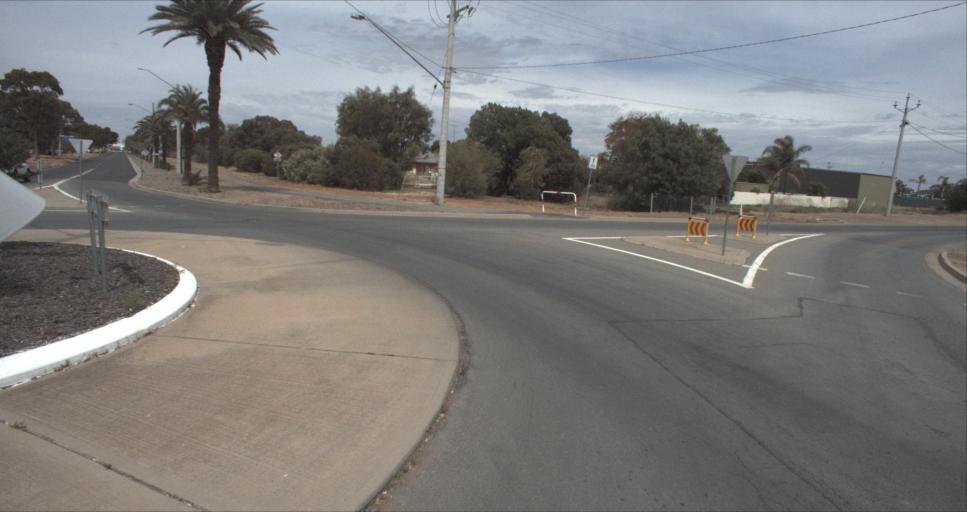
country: AU
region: New South Wales
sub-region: Leeton
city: Leeton
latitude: -34.5474
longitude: 146.4013
